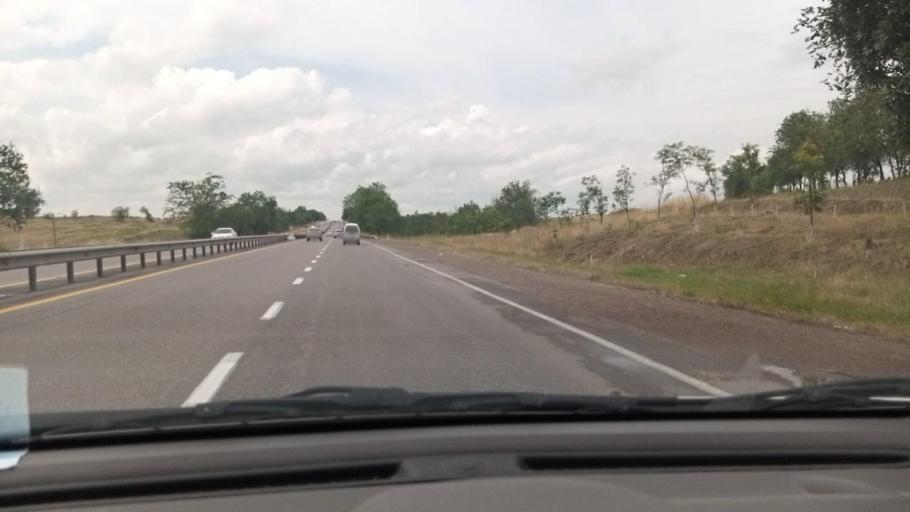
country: UZ
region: Toshkent
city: Ohangaron
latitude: 41.0076
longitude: 69.5216
